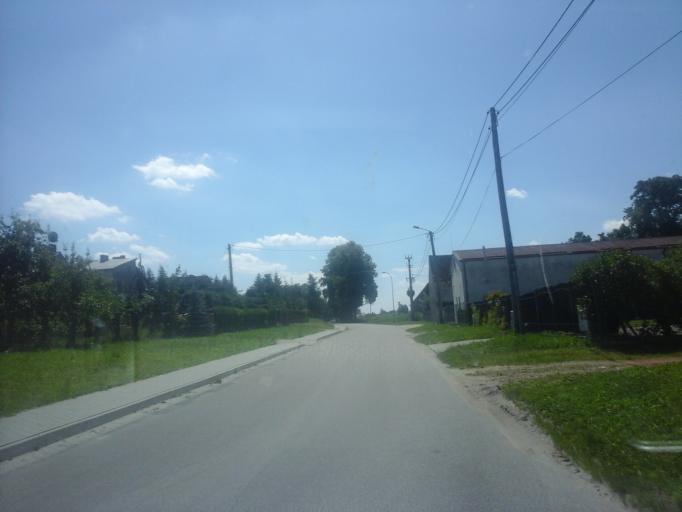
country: PL
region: West Pomeranian Voivodeship
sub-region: Powiat bialogardzki
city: Bialogard
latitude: 54.0253
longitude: 15.9875
